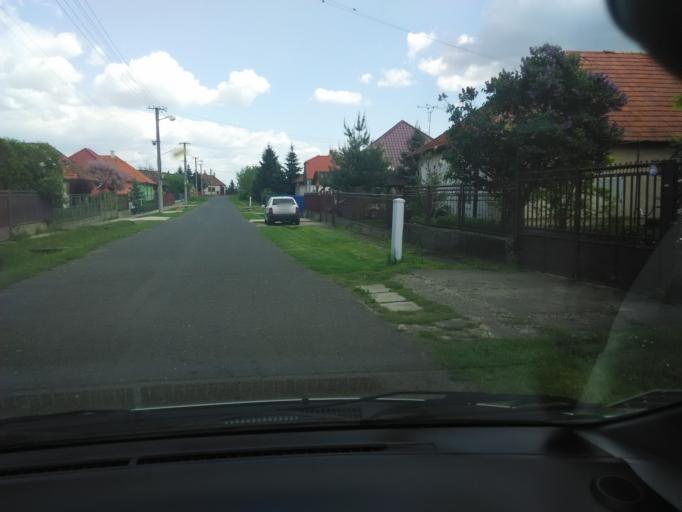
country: SK
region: Nitriansky
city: Levice
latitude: 48.1348
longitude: 18.4642
